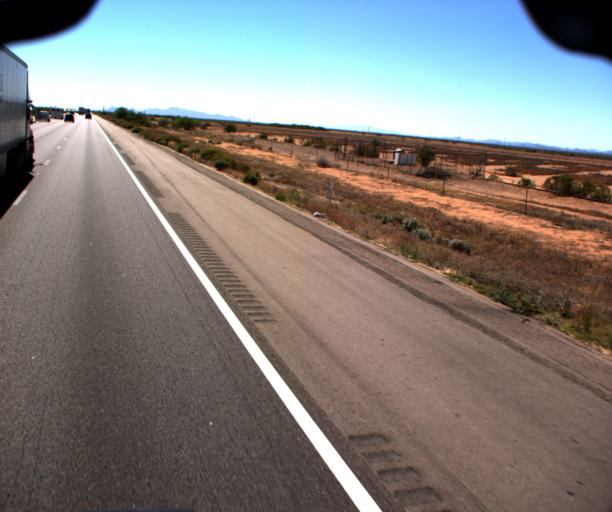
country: US
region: Arizona
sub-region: Pima County
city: Avra Valley
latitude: 32.6250
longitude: -111.3666
